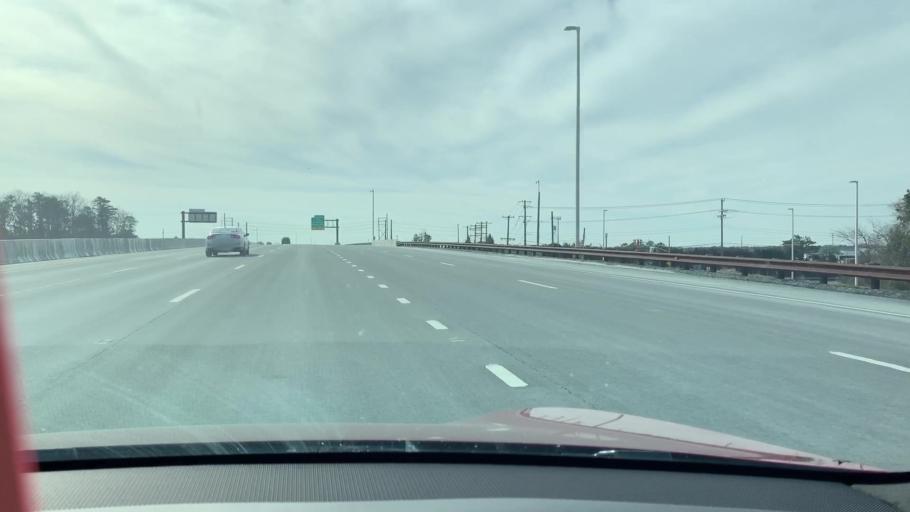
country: US
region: New Jersey
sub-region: Atlantic County
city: Northfield
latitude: 39.4060
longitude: -74.5570
